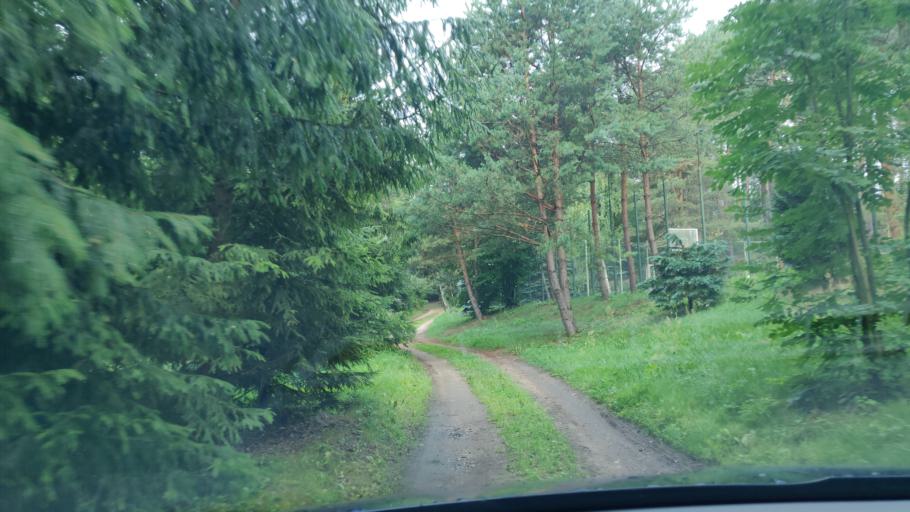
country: LT
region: Vilnius County
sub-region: Trakai
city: Rudiskes
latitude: 54.6104
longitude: 24.8232
